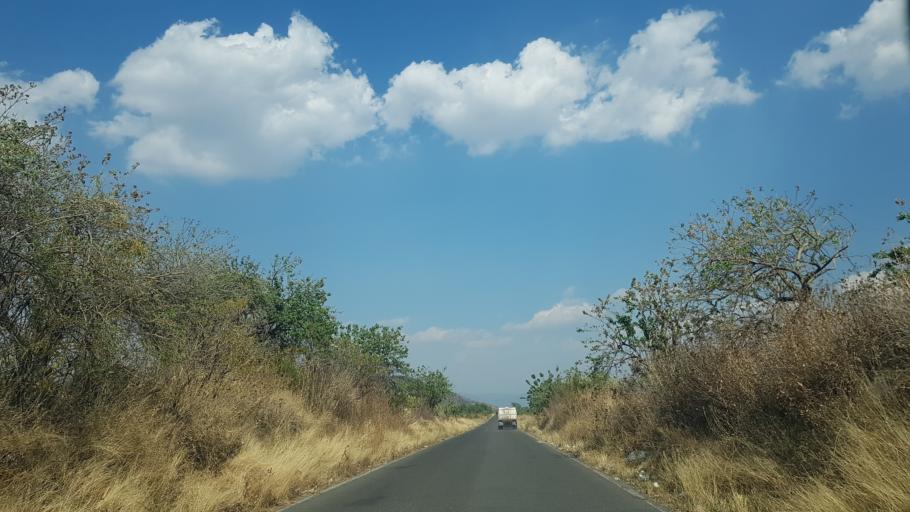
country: MX
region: Puebla
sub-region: Atlixco
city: Colonia Agricola de Ocotepec (Colonia San Jose)
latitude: 18.9236
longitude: -98.4991
